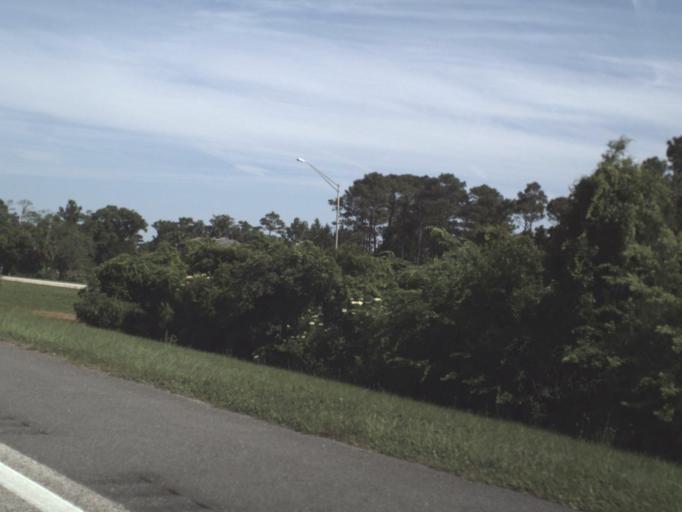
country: US
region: Florida
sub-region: Saint Johns County
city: Ponte Vedra Beach
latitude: 30.2567
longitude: -81.4024
